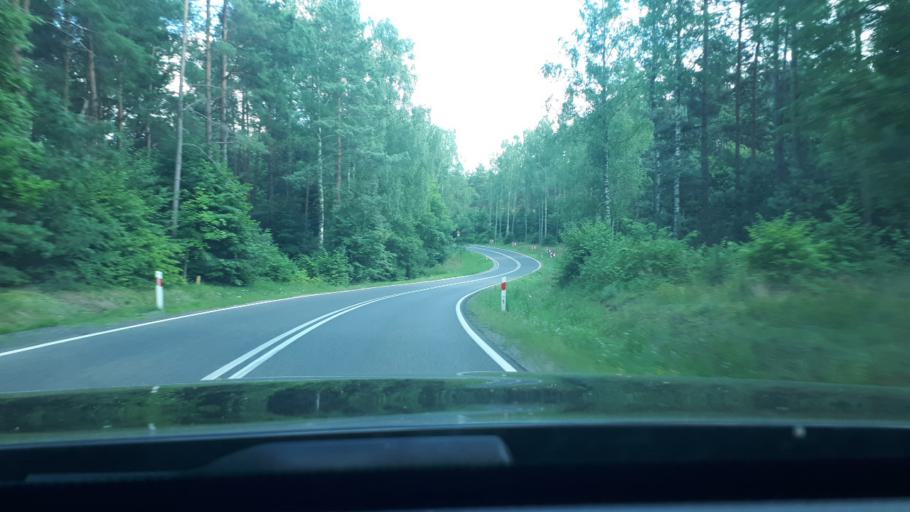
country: PL
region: Warmian-Masurian Voivodeship
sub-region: Powiat olsztynski
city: Stawiguda
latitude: 53.5299
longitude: 20.4407
